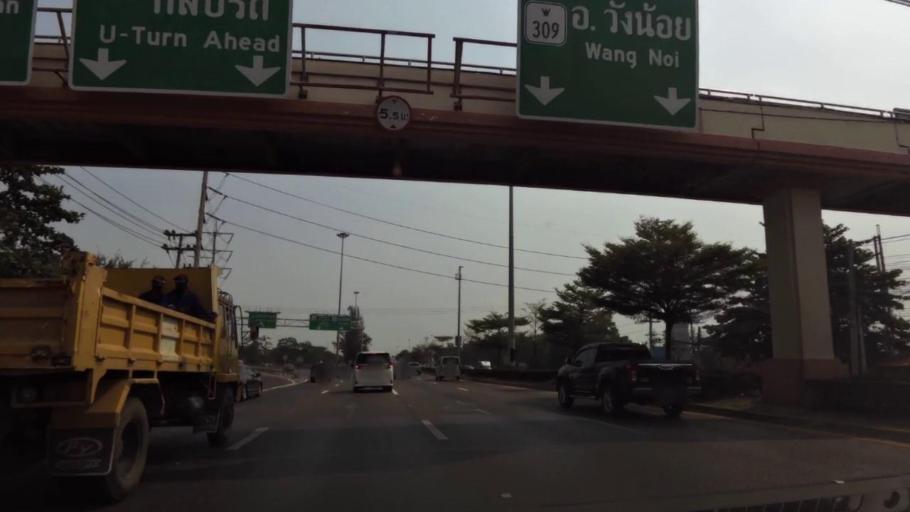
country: TH
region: Phra Nakhon Si Ayutthaya
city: Phra Nakhon Si Ayutthaya
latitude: 14.3434
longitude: 100.6102
